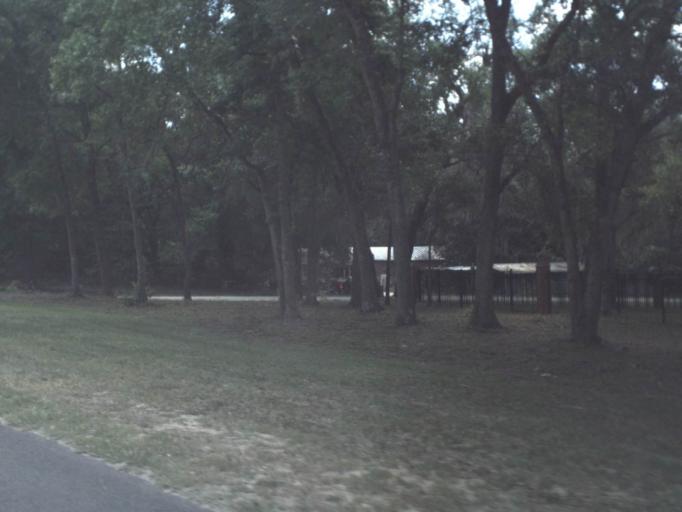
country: US
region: Florida
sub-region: Putnam County
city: Interlachen
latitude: 29.6127
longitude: -81.9870
